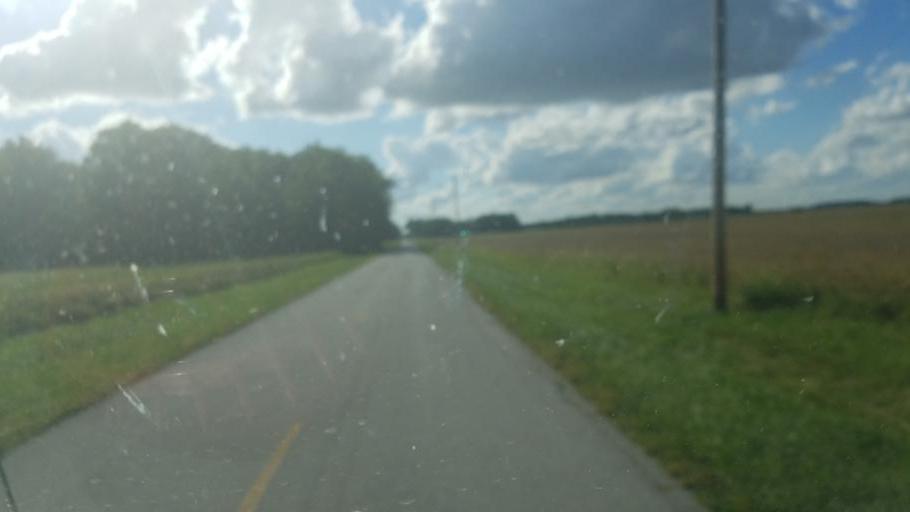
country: US
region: Ohio
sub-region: Hardin County
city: Ada
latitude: 40.7473
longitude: -83.7346
